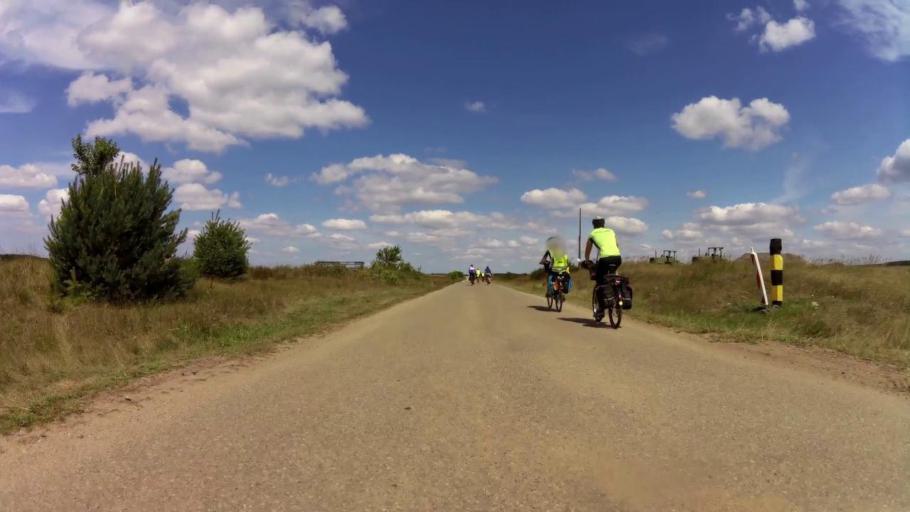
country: PL
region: West Pomeranian Voivodeship
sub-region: Powiat drawski
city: Drawsko Pomorskie
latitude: 53.4319
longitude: 15.7614
